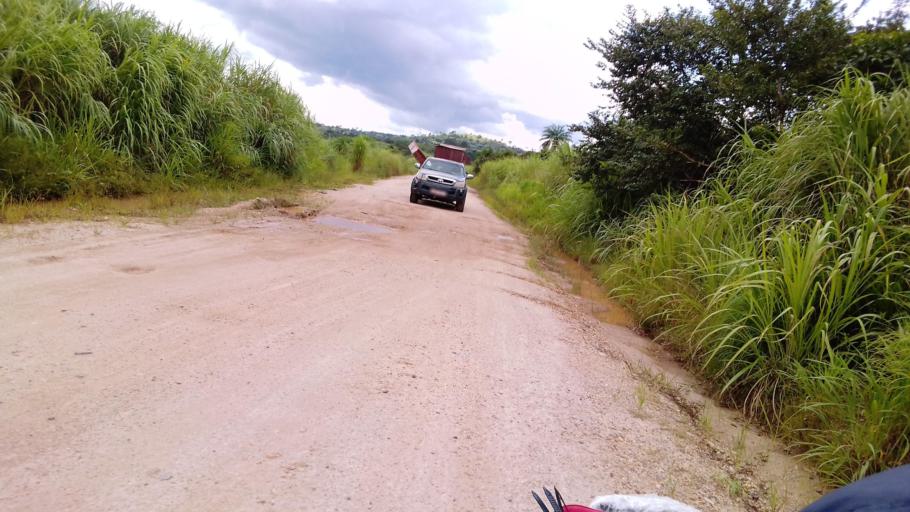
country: SL
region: Eastern Province
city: Koidu
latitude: 8.6733
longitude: -10.9878
